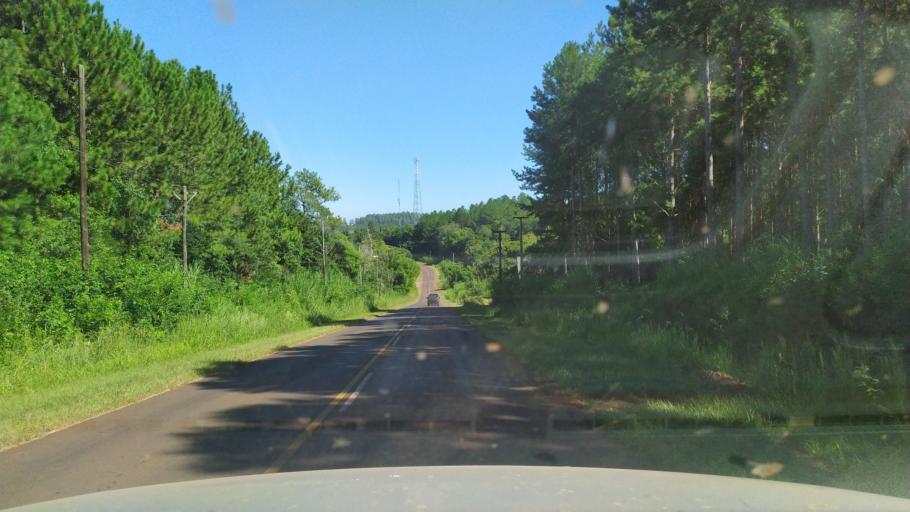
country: AR
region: Misiones
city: Caraguatay
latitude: -26.6613
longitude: -54.7347
